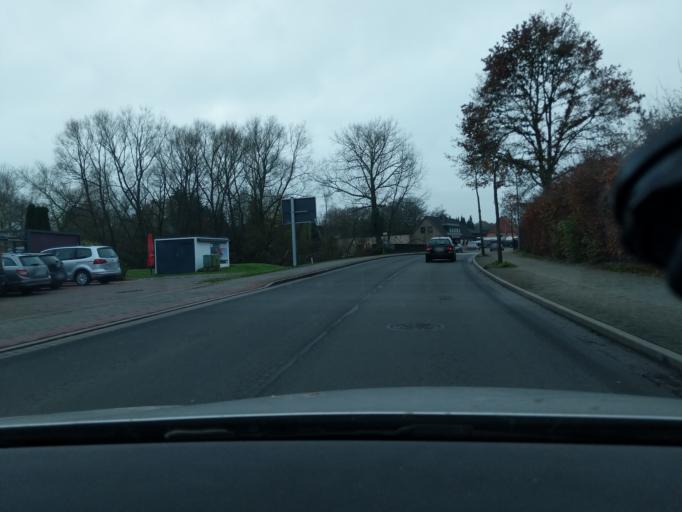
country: DE
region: Lower Saxony
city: Heeslingen
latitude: 53.3142
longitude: 9.3344
